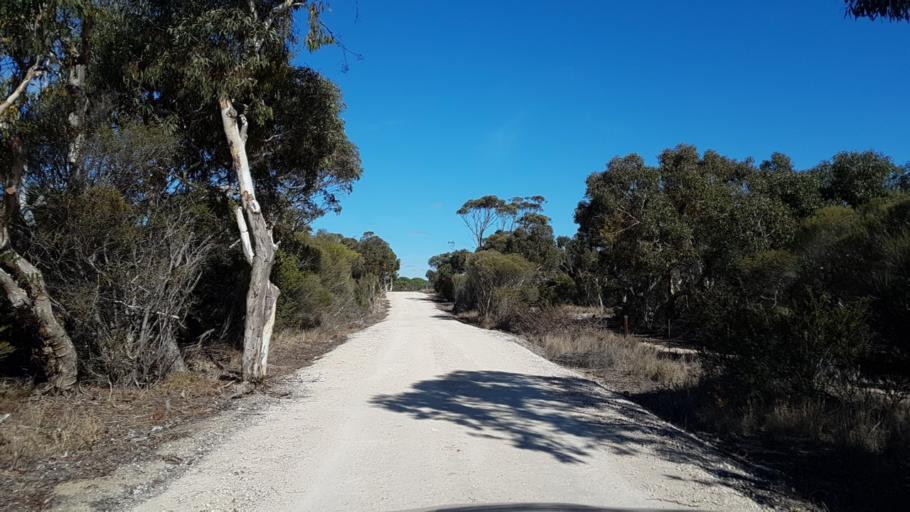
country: AU
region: South Australia
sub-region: Alexandrina
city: Goolwa
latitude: -35.3788
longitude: 138.8307
